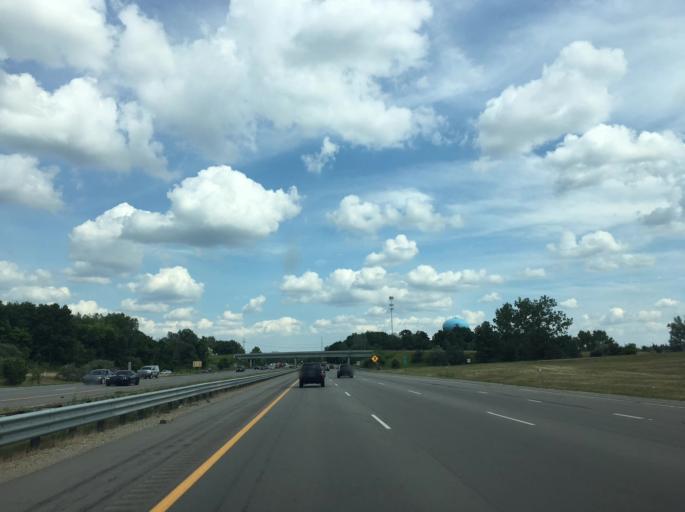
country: US
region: Michigan
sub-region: Oakland County
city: Clarkston
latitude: 42.7355
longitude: -83.3791
